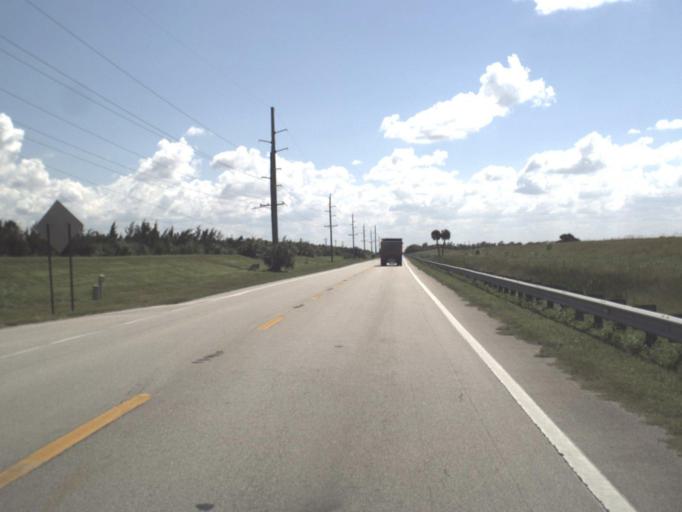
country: US
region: Florida
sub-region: Glades County
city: Moore Haven
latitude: 26.8811
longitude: -81.1226
